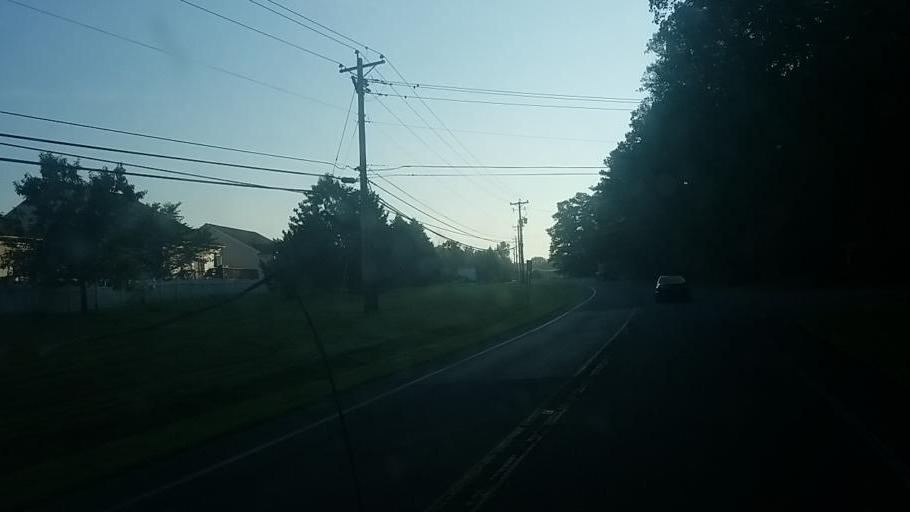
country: US
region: Delaware
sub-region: Sussex County
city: Selbyville
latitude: 38.4559
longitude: -75.2054
